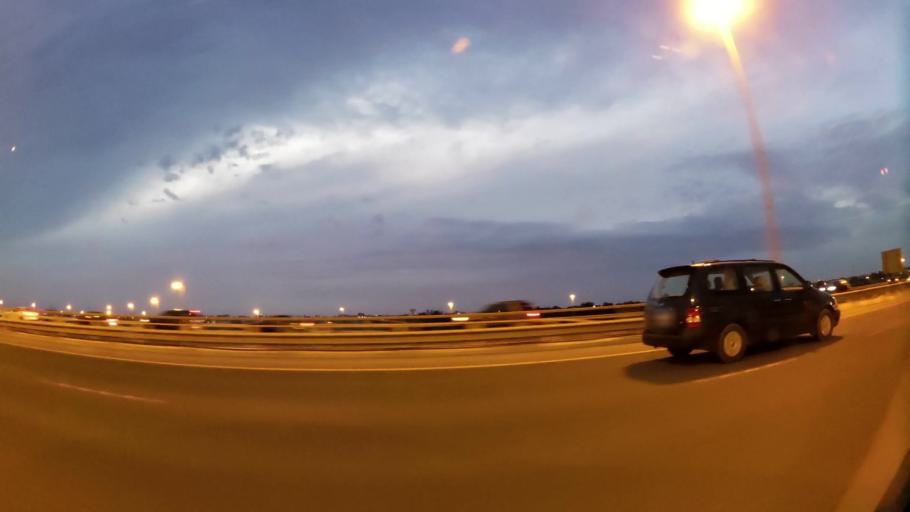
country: BH
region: Northern
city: Madinat `Isa
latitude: 26.1884
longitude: 50.5041
